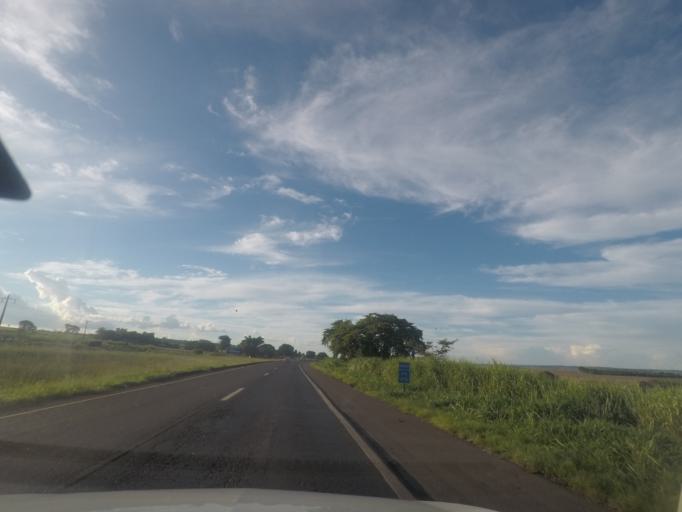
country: BR
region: Goias
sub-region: Goiatuba
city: Goiatuba
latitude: -18.1857
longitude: -49.2889
